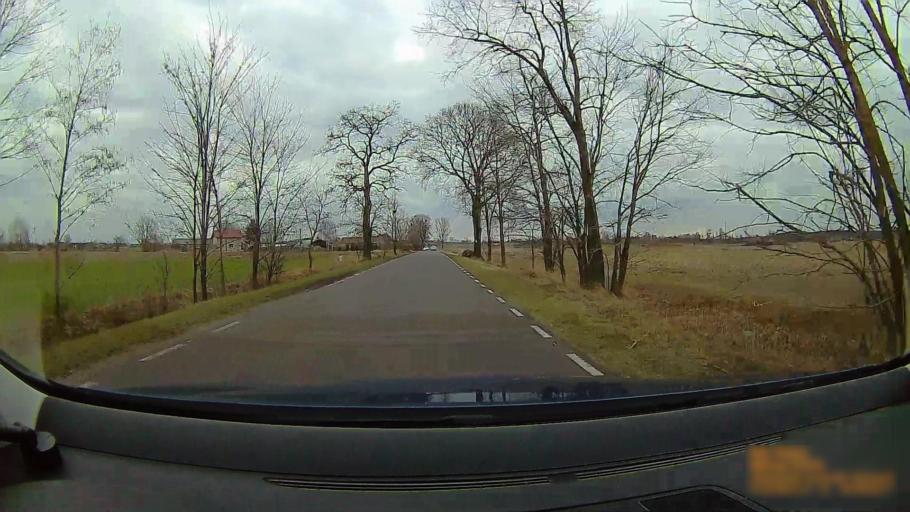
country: PL
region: Greater Poland Voivodeship
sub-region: Powiat koninski
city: Rzgow Pierwszy
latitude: 52.1113
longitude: 18.0760
